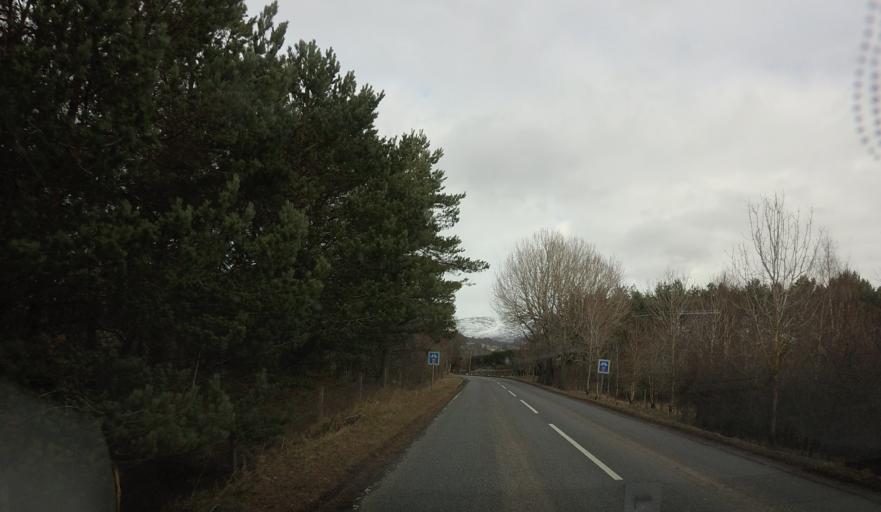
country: GB
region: Scotland
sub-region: Highland
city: Kingussie
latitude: 57.0534
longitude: -4.1306
